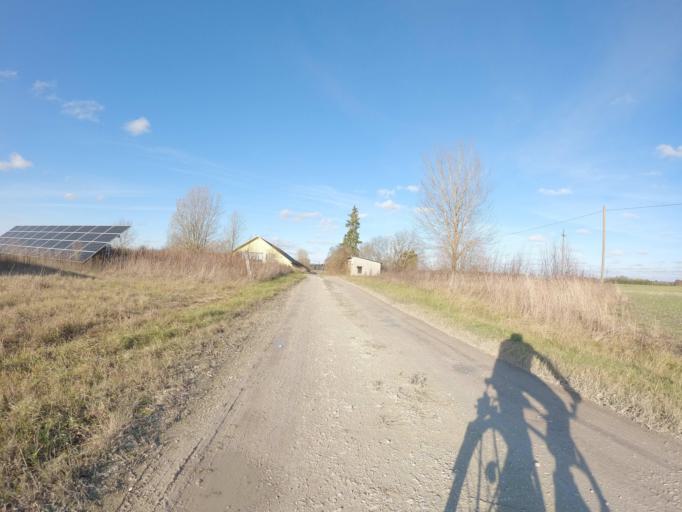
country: EE
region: Raplamaa
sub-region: Rapla vald
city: Rapla
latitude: 59.0264
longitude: 24.7939
